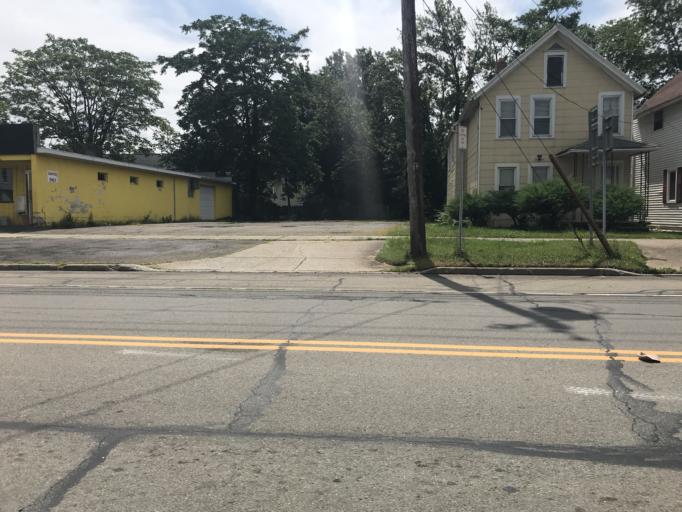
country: US
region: New York
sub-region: Chautauqua County
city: Dunkirk
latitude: 42.4883
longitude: -79.3289
